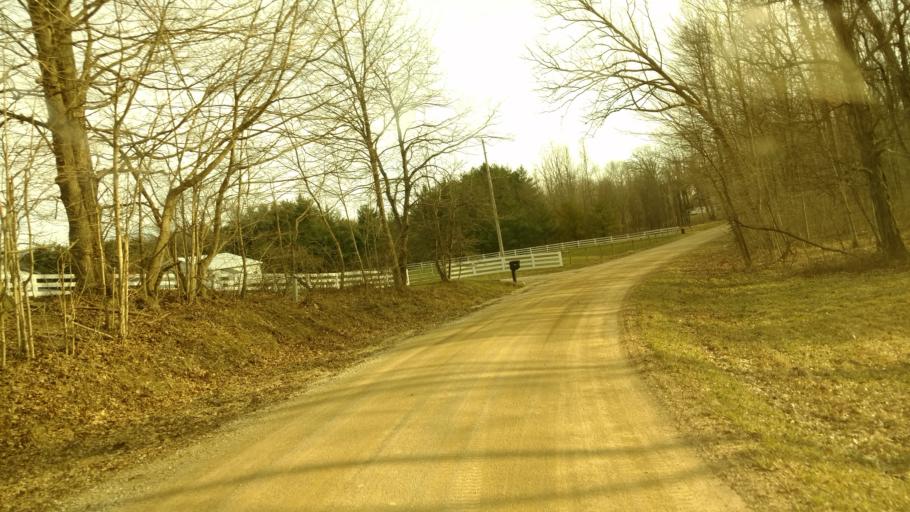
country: US
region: Ohio
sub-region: Knox County
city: Danville
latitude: 40.5503
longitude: -82.3277
